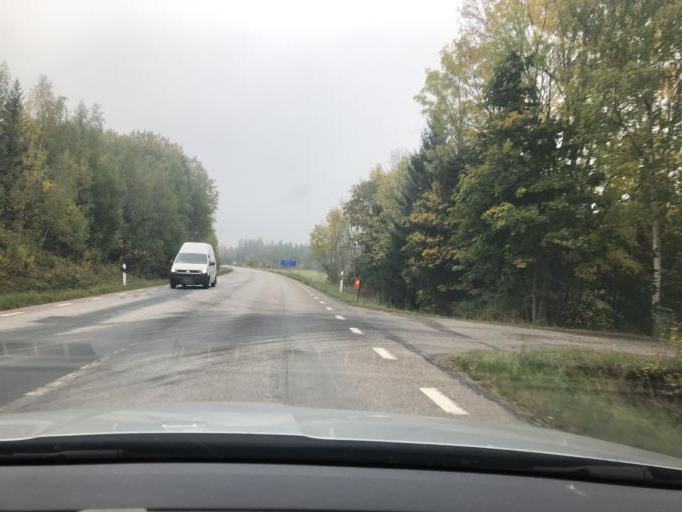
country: SE
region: Uppsala
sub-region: Tierps Kommun
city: Orbyhus
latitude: 60.2184
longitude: 17.6951
